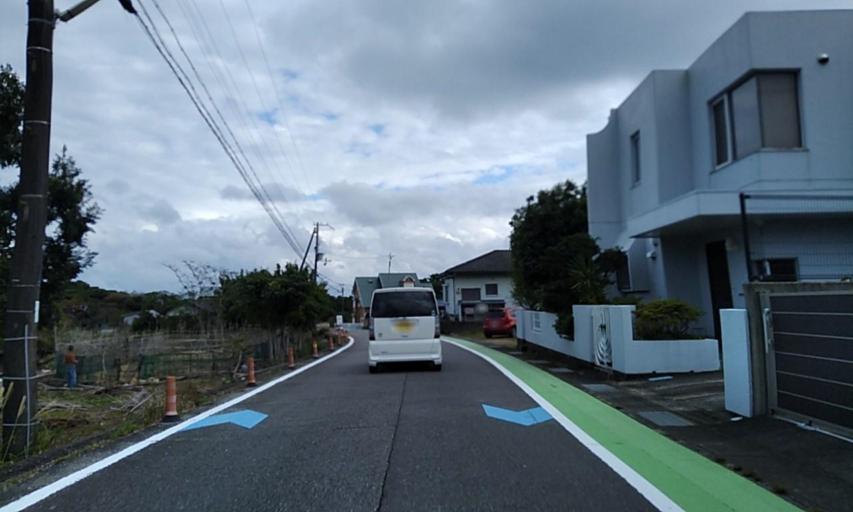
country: JP
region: Wakayama
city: Shingu
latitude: 33.5848
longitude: 135.9505
